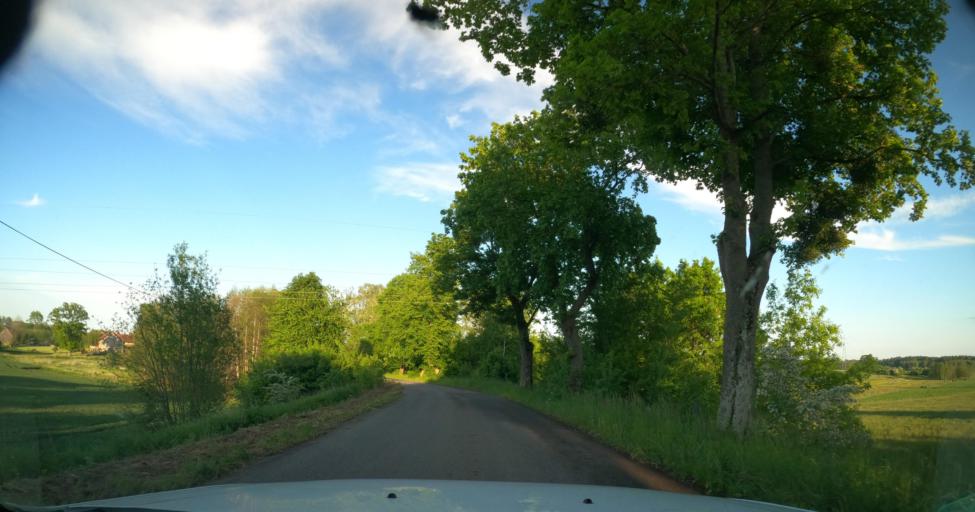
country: PL
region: Warmian-Masurian Voivodeship
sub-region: Powiat lidzbarski
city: Orneta
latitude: 54.1745
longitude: 20.1456
